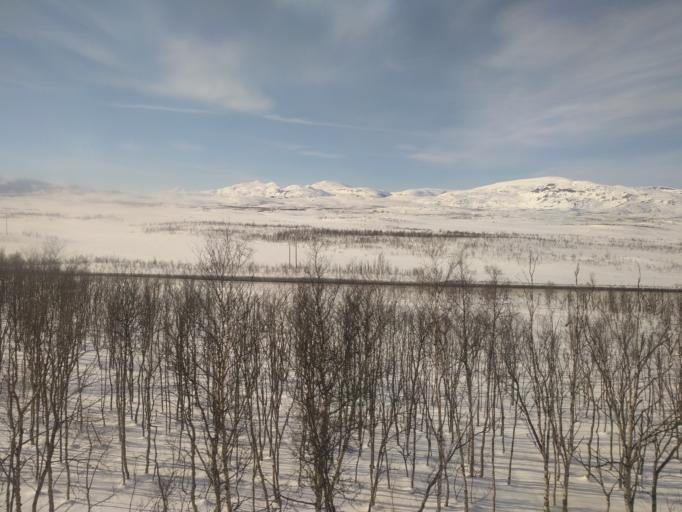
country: NO
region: Troms
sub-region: Bardu
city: Setermoen
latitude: 68.4266
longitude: 18.3934
